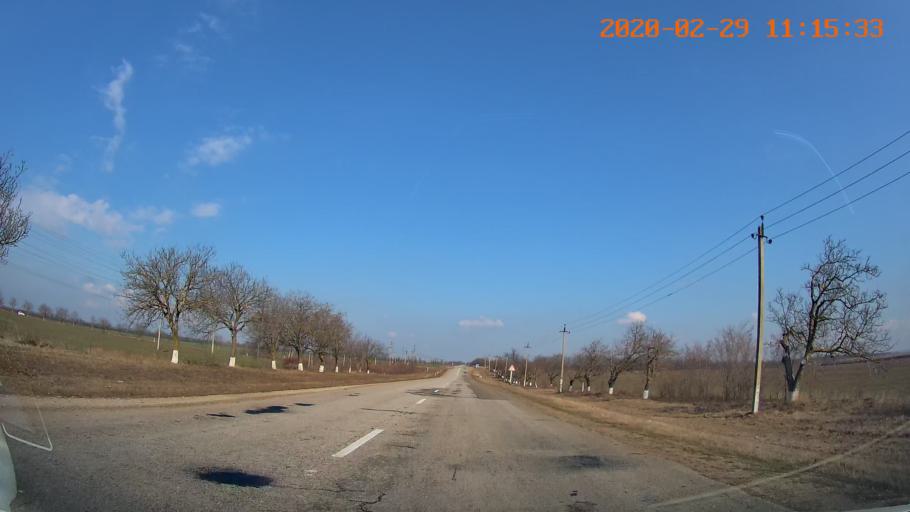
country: MD
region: Telenesti
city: Dubasari
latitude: 47.2962
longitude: 29.1654
